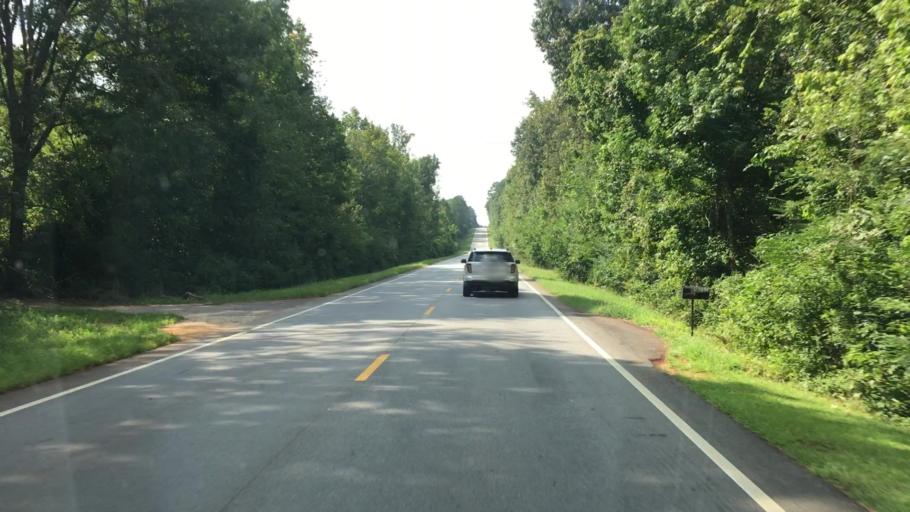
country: US
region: Georgia
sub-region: Jasper County
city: Monticello
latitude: 33.3196
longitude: -83.6963
